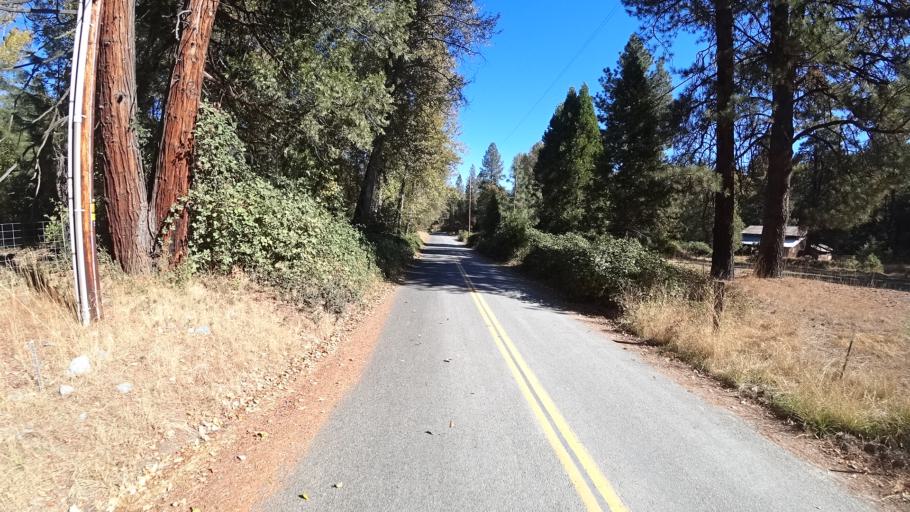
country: US
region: California
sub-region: Siskiyou County
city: Yreka
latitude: 41.5311
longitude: -122.9451
